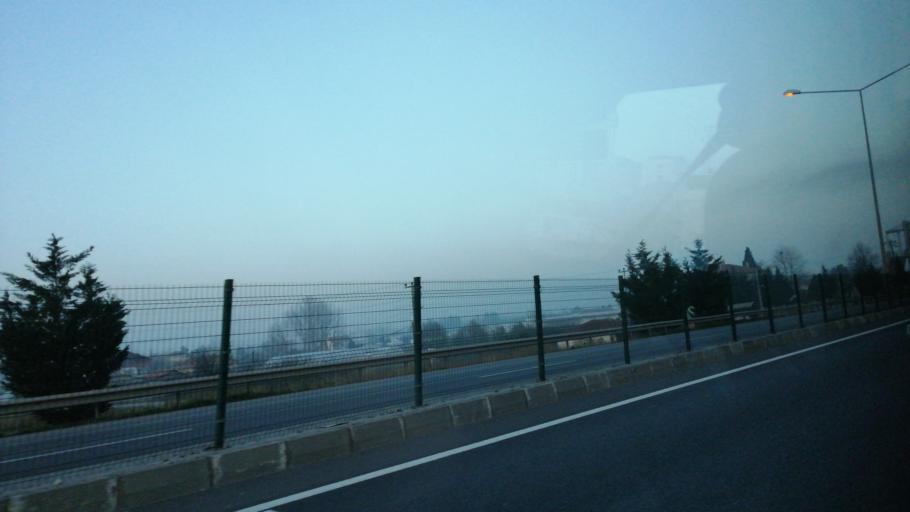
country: TR
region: Yalova
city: Altinova
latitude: 40.6874
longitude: 29.4512
